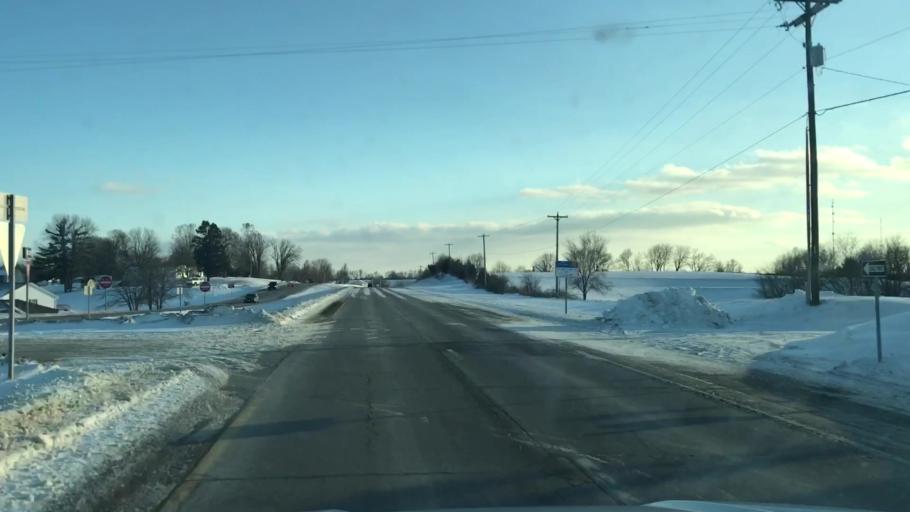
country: US
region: Missouri
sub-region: Andrew County
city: Country Club Village
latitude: 39.8718
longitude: -94.8088
